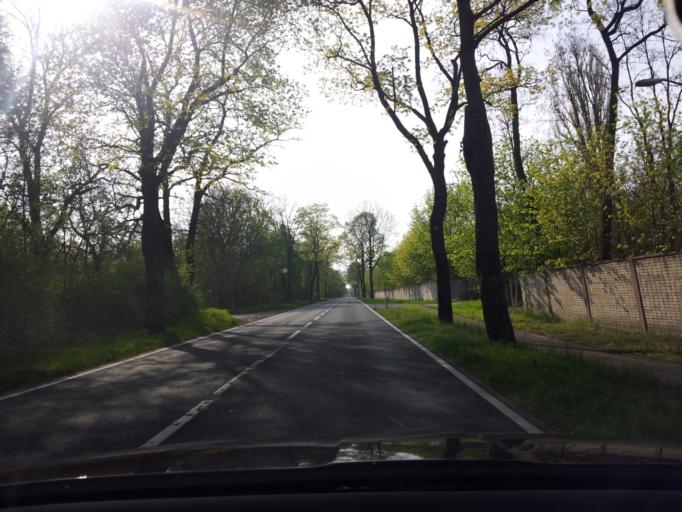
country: DE
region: Brandenburg
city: Niedergorsdorf
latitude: 52.0026
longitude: 13.0243
